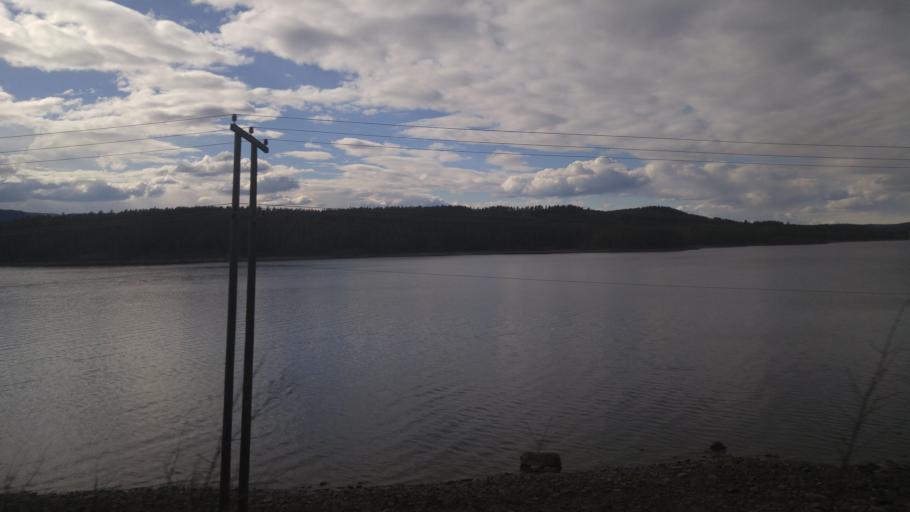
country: NO
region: Hedmark
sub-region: Stange
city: Stange
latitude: 60.5885
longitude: 11.2818
